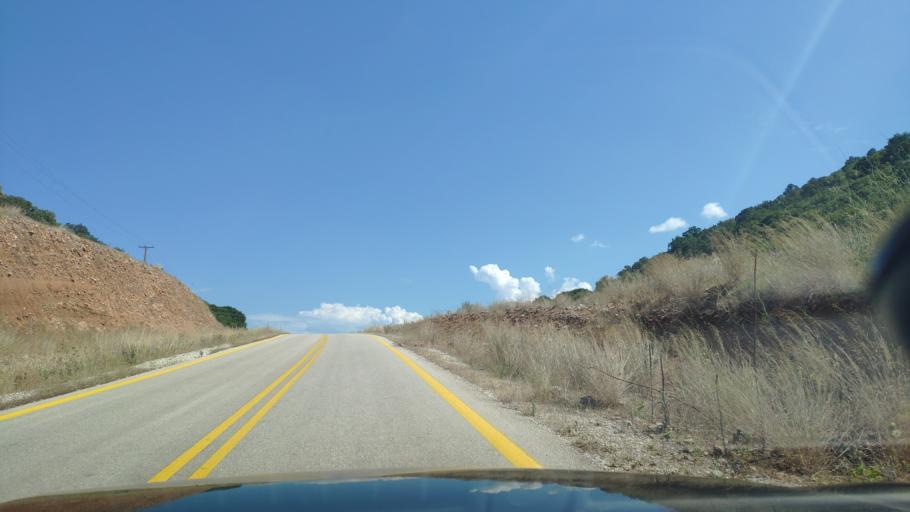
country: GR
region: West Greece
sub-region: Nomos Aitolias kai Akarnanias
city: Katouna
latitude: 38.8571
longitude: 21.0863
